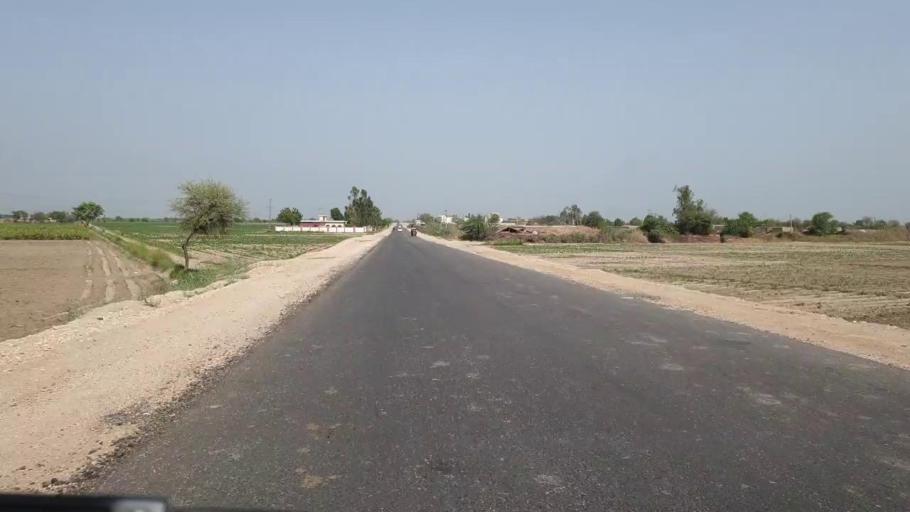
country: PK
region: Sindh
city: Sakrand
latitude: 26.2649
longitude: 68.1751
